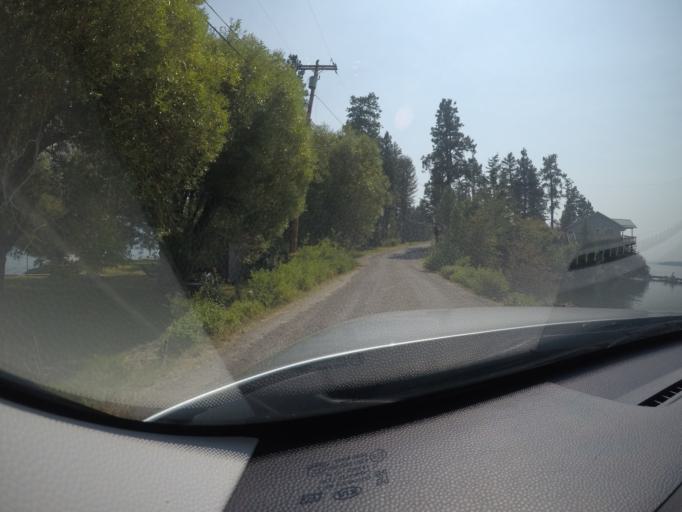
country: US
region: Montana
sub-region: Lake County
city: Polson
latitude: 47.7671
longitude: -114.1424
